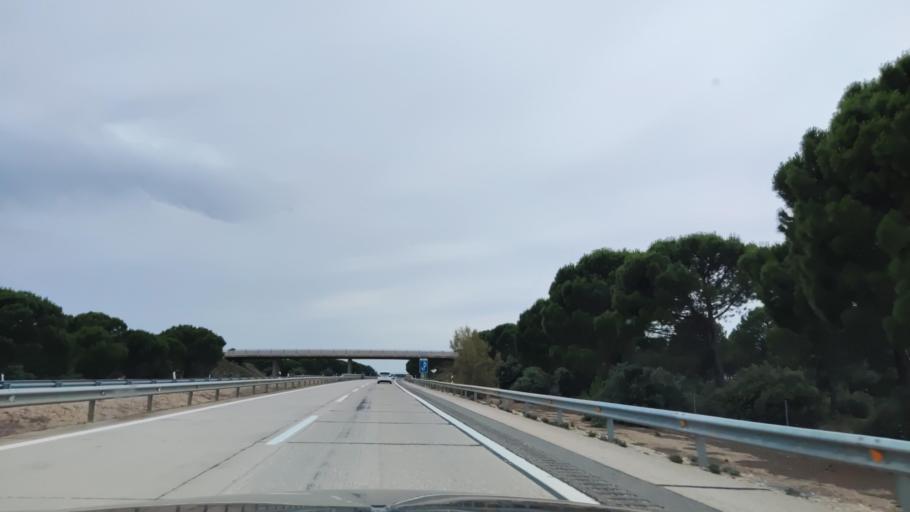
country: ES
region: Castille-La Mancha
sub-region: Provincia de Cuenca
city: Pozoamargo
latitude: 39.3329
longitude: -2.2003
